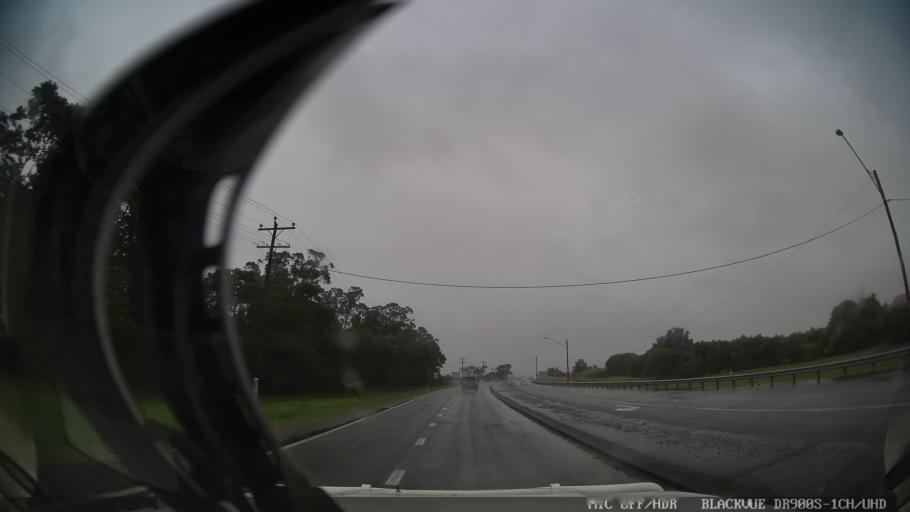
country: AU
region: Queensland
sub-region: Cassowary Coast
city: Innisfail
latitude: -17.7473
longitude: 146.0277
